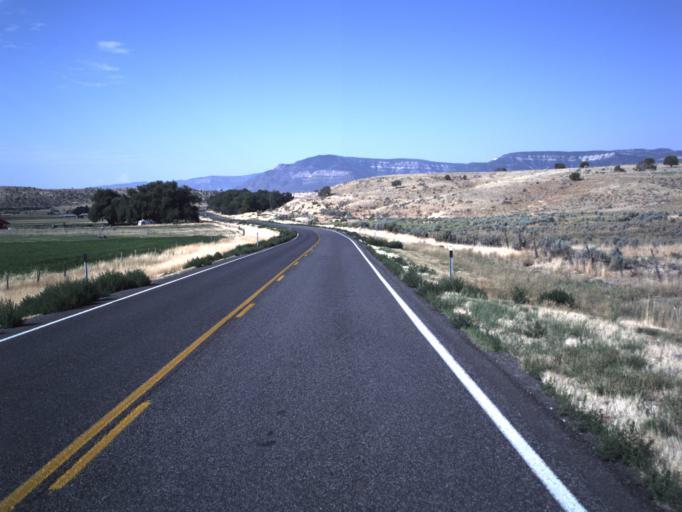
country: US
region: Utah
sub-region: Sanpete County
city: Moroni
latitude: 39.5369
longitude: -111.5388
